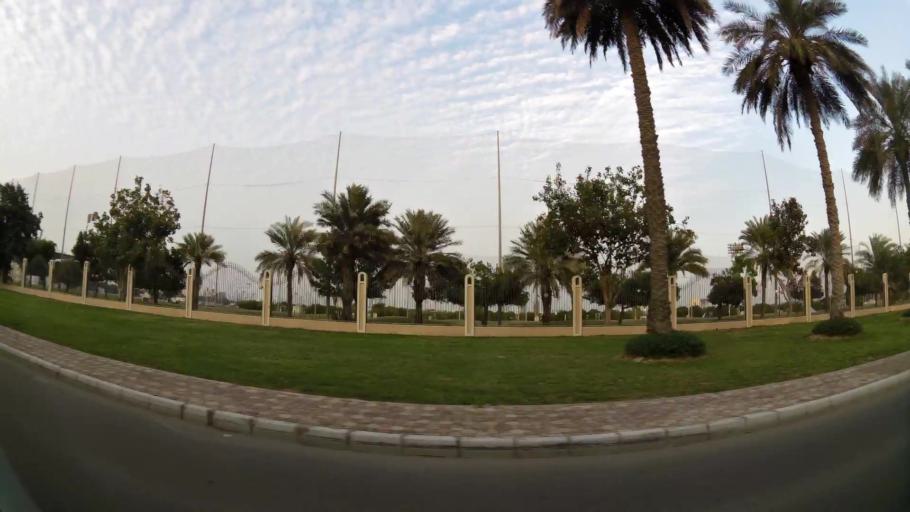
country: AE
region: Abu Dhabi
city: Abu Dhabi
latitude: 24.4408
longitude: 54.3761
